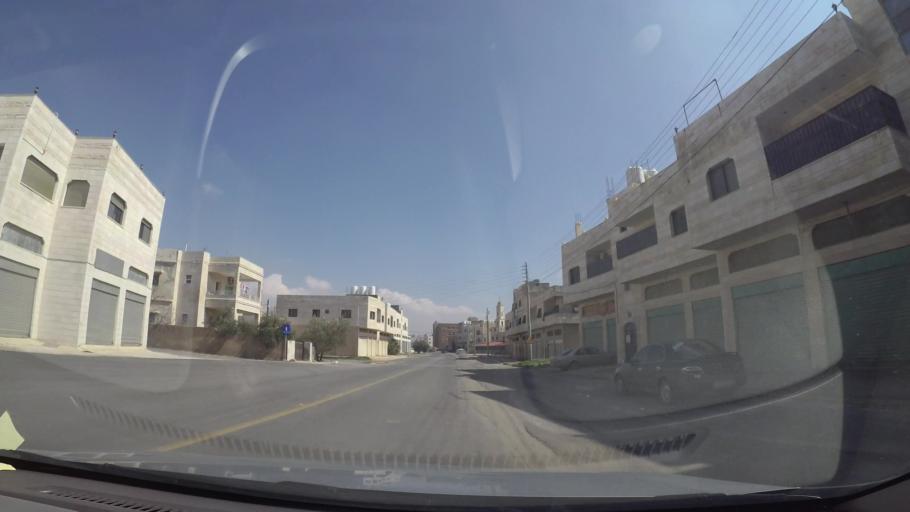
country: JO
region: Amman
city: Al Bunayyat ash Shamaliyah
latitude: 31.8986
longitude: 35.9011
